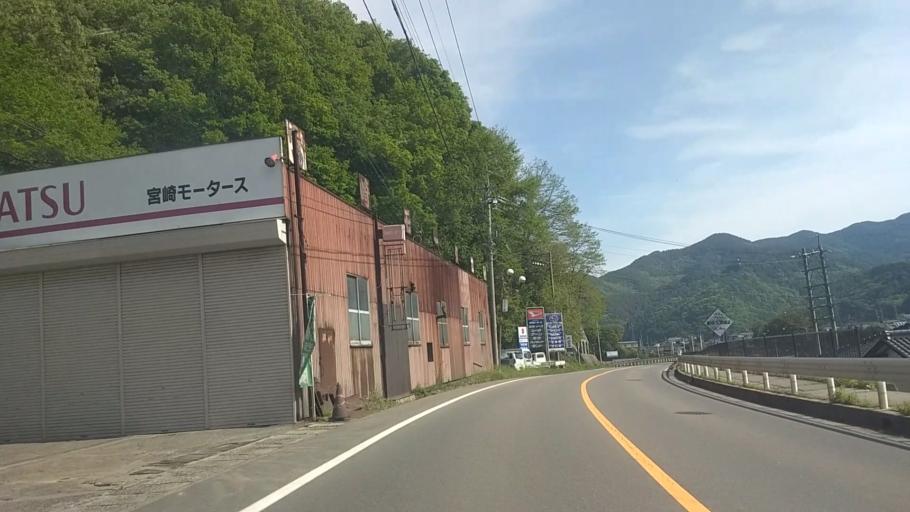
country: JP
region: Nagano
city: Saku
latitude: 36.0975
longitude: 138.4821
